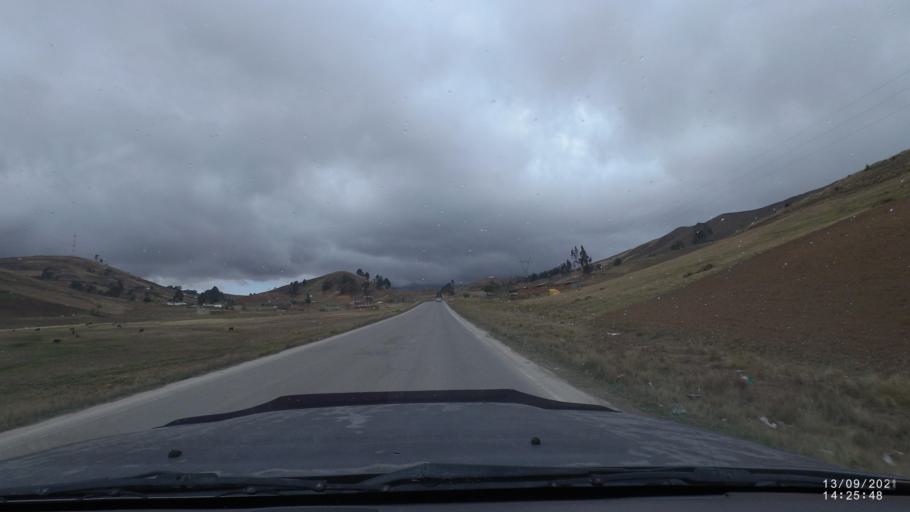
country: BO
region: Cochabamba
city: Colomi
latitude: -17.3000
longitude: -65.8700
